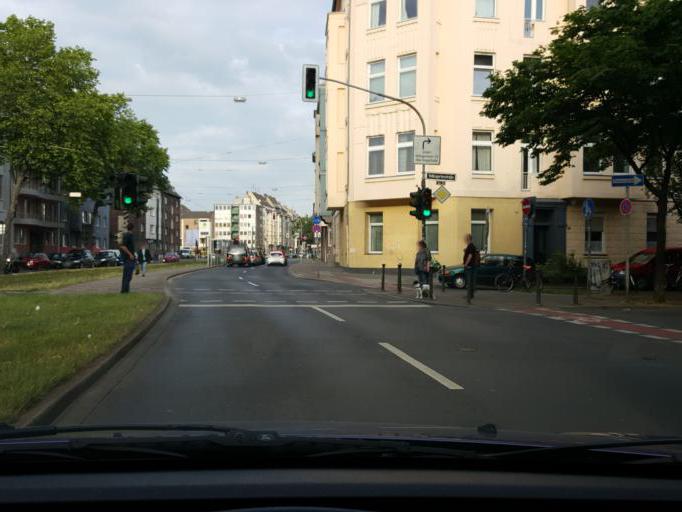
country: DE
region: North Rhine-Westphalia
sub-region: Regierungsbezirk Dusseldorf
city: Dusseldorf
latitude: 51.2113
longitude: 6.7933
